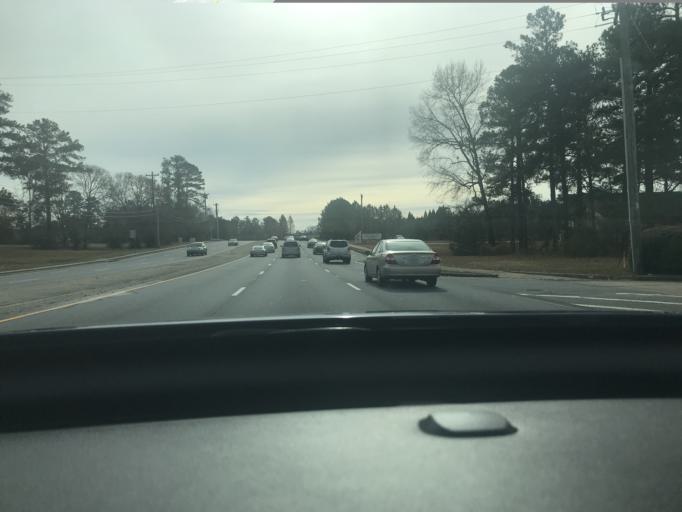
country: US
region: Georgia
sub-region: Gwinnett County
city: Lilburn
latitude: 33.9175
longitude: -84.1137
